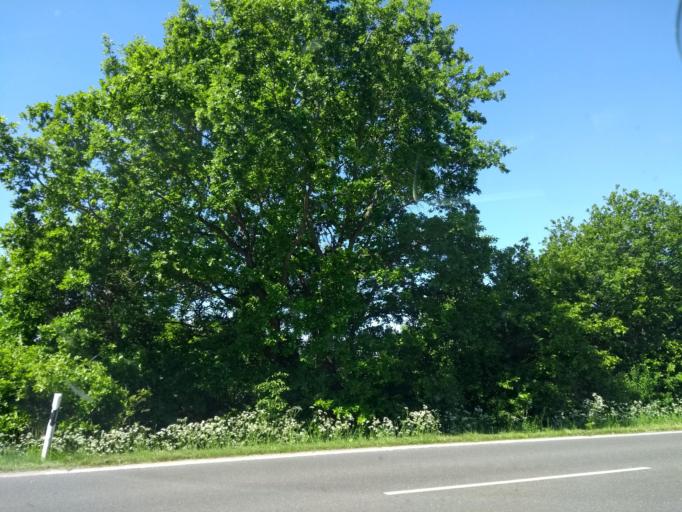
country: DE
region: Schleswig-Holstein
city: Eckernforde
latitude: 54.4873
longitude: 9.8556
